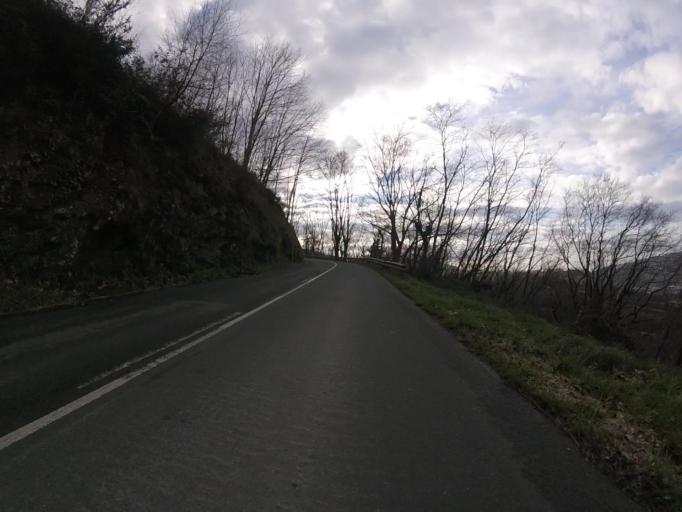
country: ES
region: Basque Country
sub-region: Provincia de Guipuzcoa
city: Irun
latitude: 43.3219
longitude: -1.8219
